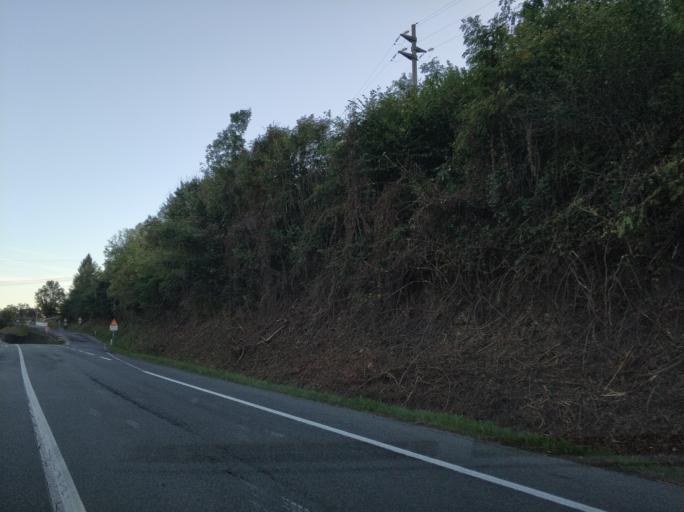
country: IT
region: Piedmont
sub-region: Provincia di Torino
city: Fiano
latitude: 45.2315
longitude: 7.5259
